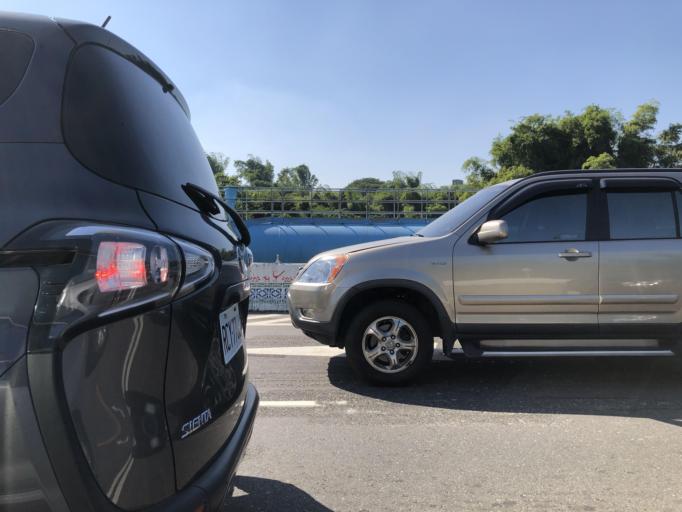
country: TW
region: Taiwan
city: Yujing
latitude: 23.0551
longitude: 120.4021
